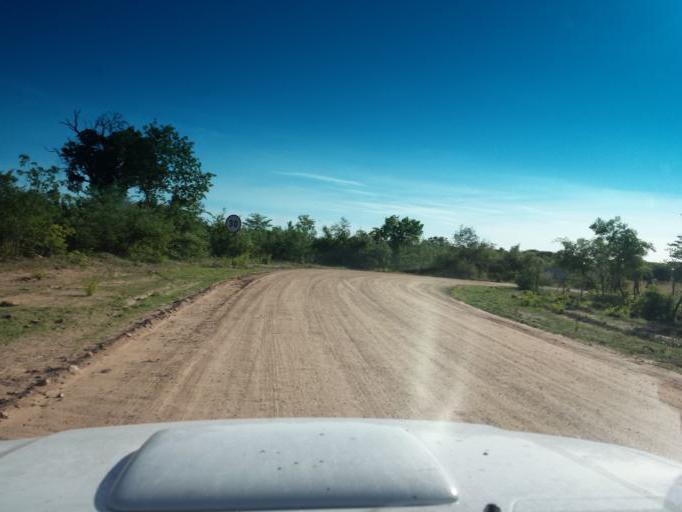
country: BW
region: North West
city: Shakawe
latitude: -18.2570
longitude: 21.7593
